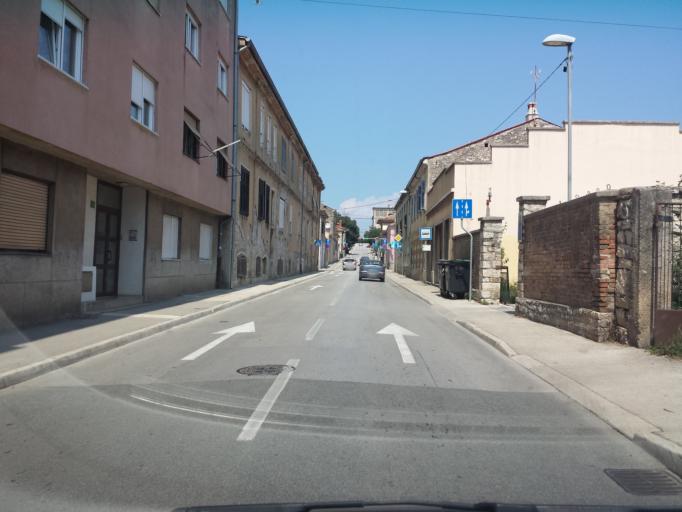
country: HR
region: Istarska
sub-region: Grad Pula
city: Pula
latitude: 44.8685
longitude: 13.8528
